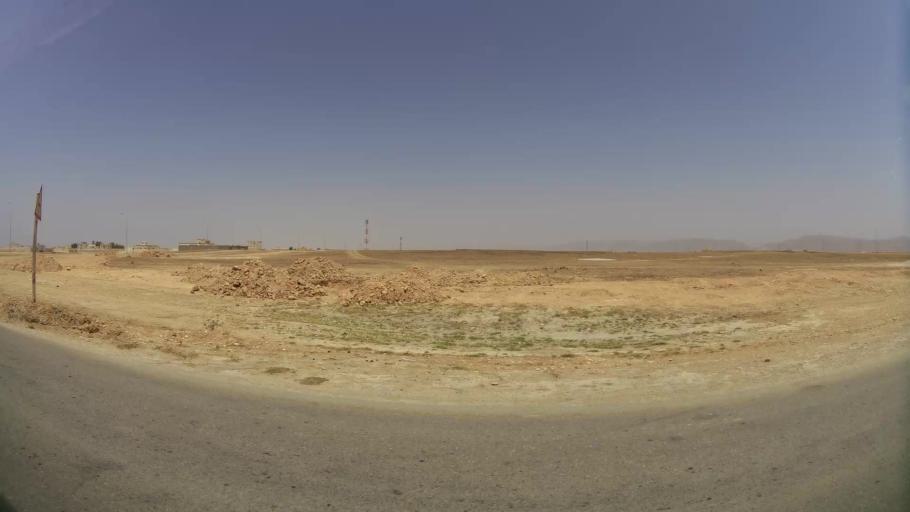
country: OM
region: Zufar
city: Salalah
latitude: 17.0926
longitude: 54.1924
